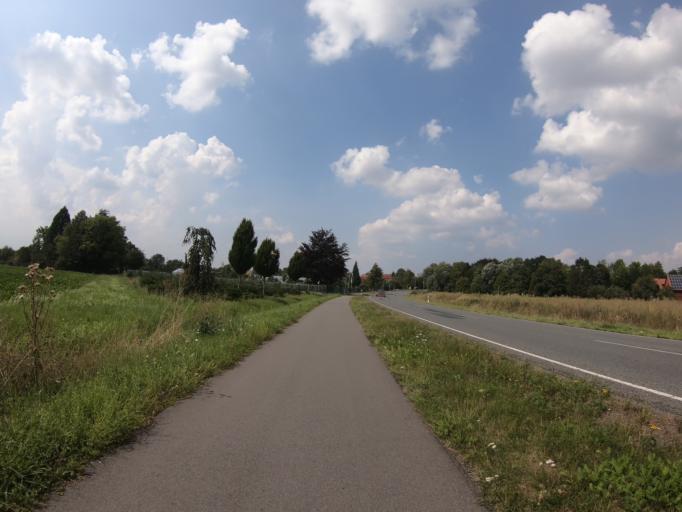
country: DE
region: Lower Saxony
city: Sickte
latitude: 52.2151
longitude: 10.6477
